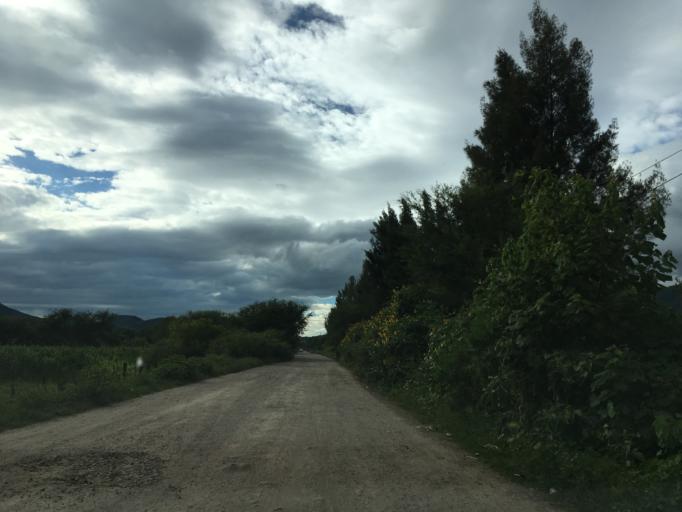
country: MX
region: Guanajuato
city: Iramuco
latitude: 19.9643
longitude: -100.9400
